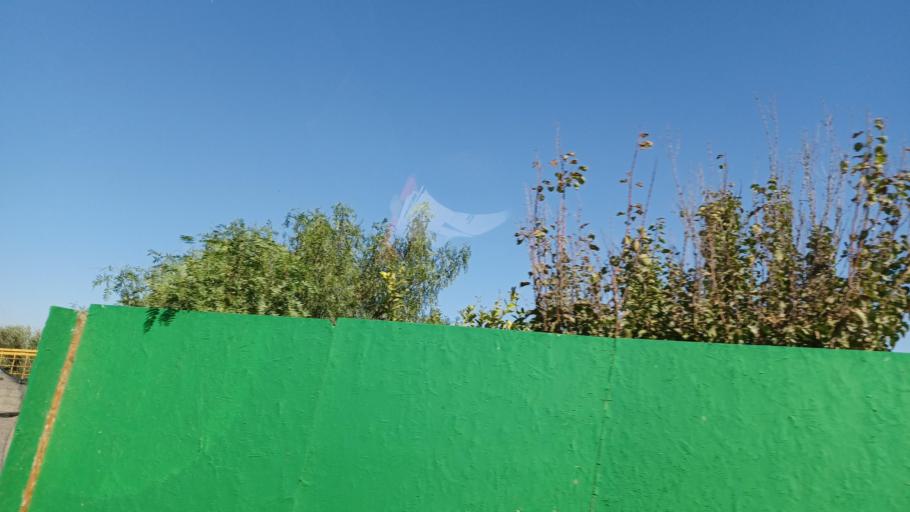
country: CY
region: Larnaka
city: Kolossi
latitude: 34.6353
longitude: 32.9262
